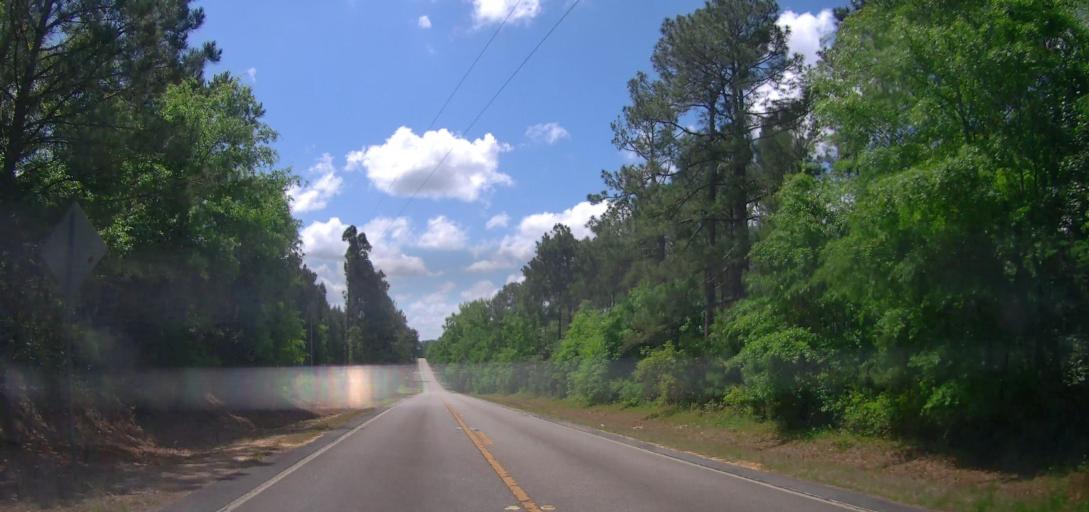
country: US
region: Georgia
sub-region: Bleckley County
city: Cochran
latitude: 32.4572
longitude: -83.2864
